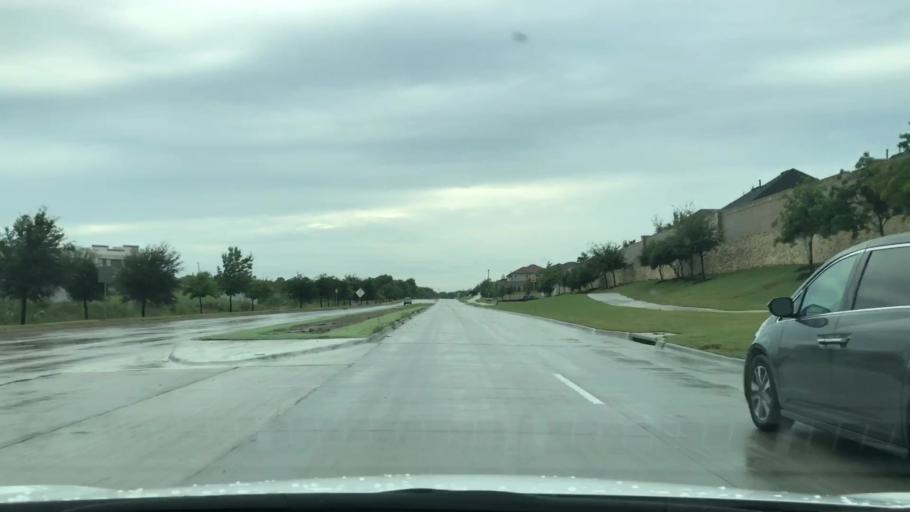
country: US
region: Texas
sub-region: Dallas County
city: Coppell
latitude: 32.9039
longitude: -96.9972
